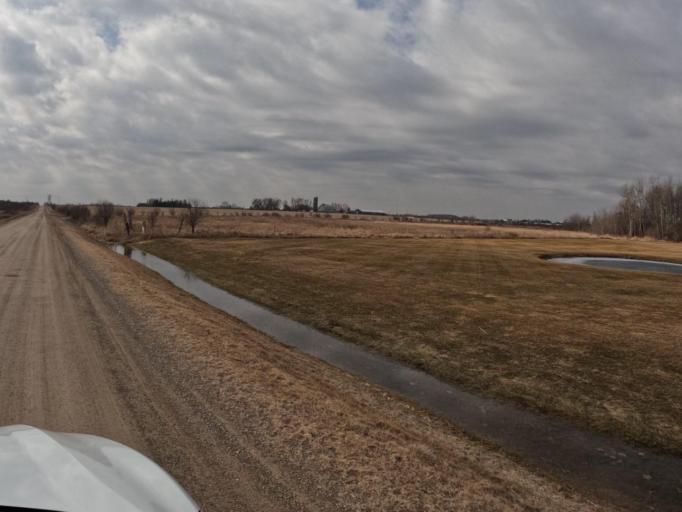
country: CA
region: Ontario
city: Orangeville
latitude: 43.9270
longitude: -80.2195
